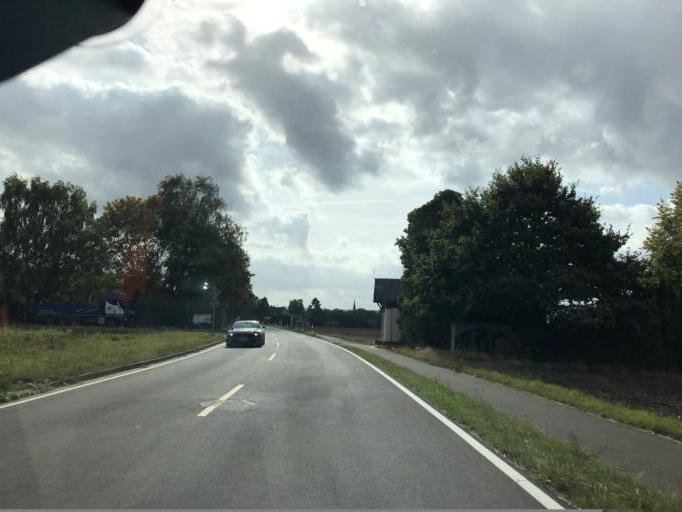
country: DE
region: North Rhine-Westphalia
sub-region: Regierungsbezirk Koln
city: Rheinbach
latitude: 50.6470
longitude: 6.9192
